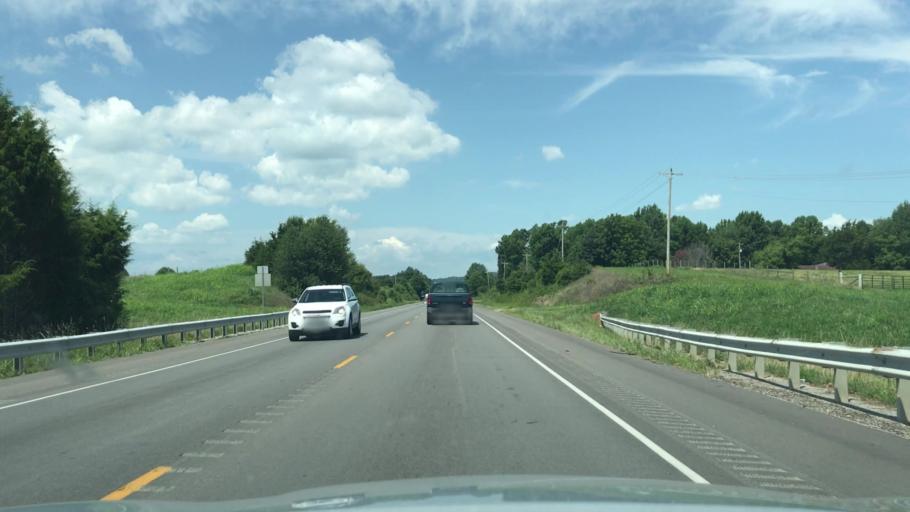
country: US
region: Kentucky
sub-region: Clinton County
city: Albany
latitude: 36.7540
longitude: -85.1270
